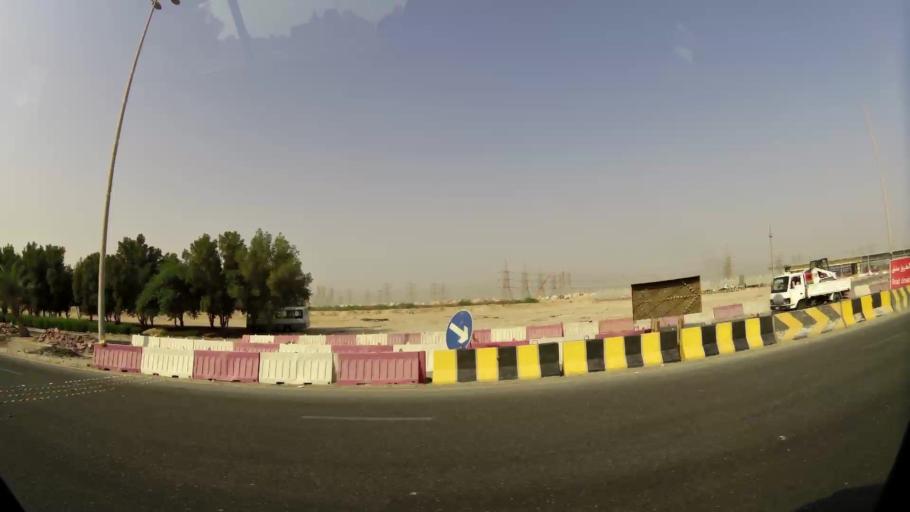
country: KW
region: Al Asimah
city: Ar Rabiyah
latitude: 29.3338
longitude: 47.7993
